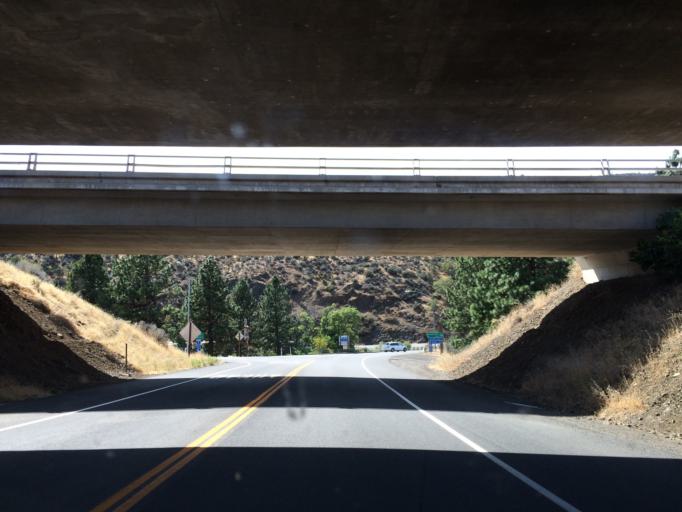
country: US
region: California
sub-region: Siskiyou County
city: Montague
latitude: 41.8550
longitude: -122.5715
